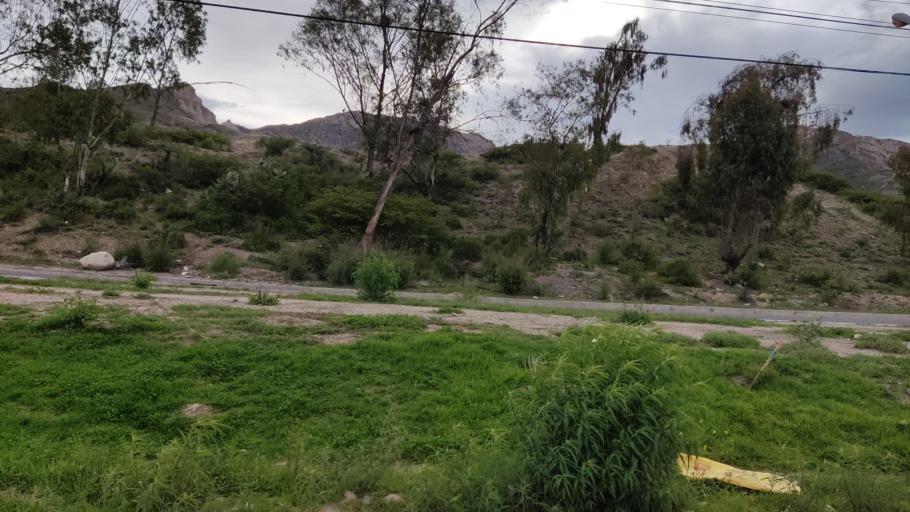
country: BO
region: La Paz
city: La Paz
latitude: -16.5853
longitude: -68.0773
